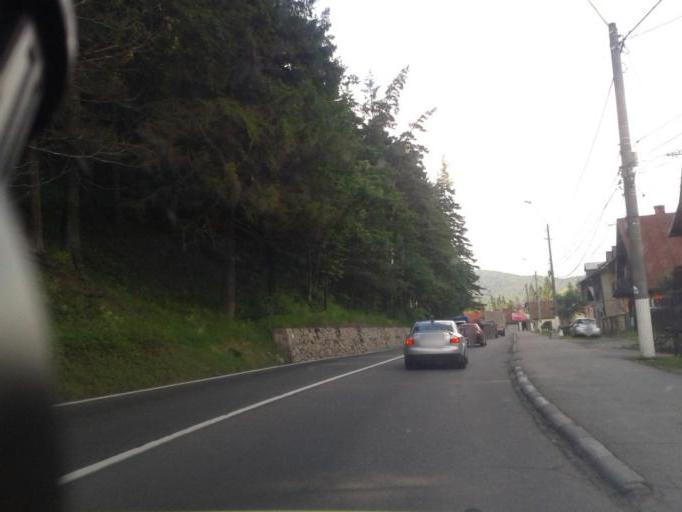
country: RO
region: Prahova
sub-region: Oras Busteni
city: Busteni
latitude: 45.4014
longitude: 25.5345
